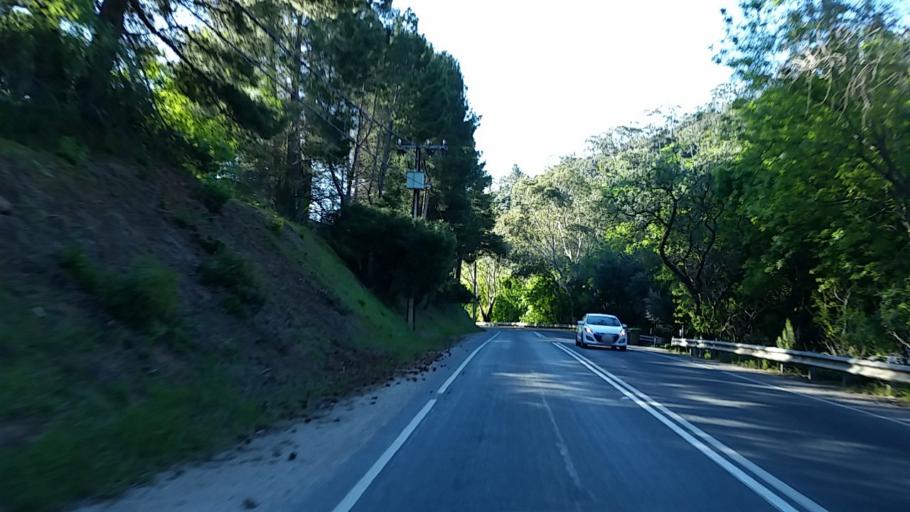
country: AU
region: South Australia
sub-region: Adelaide Hills
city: Adelaide Hills
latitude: -34.9163
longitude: 138.6938
